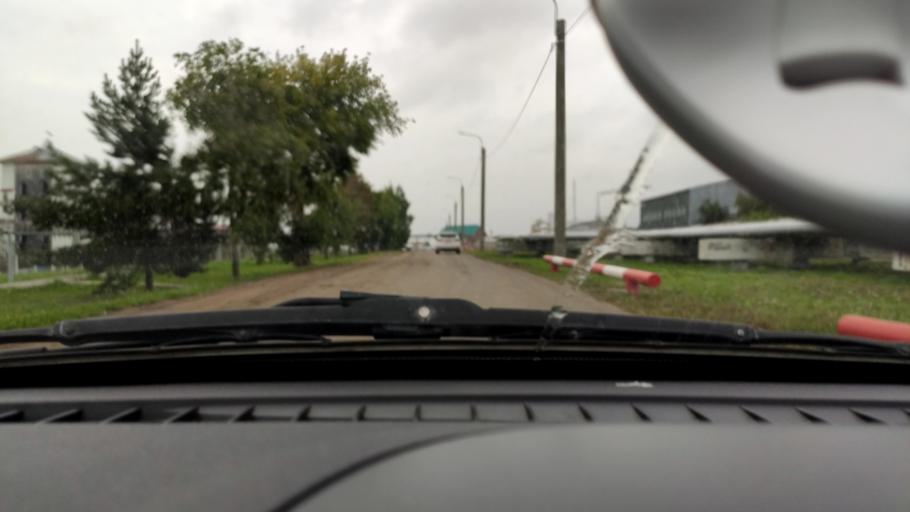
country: RU
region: Perm
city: Gamovo
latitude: 57.9100
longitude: 56.1469
